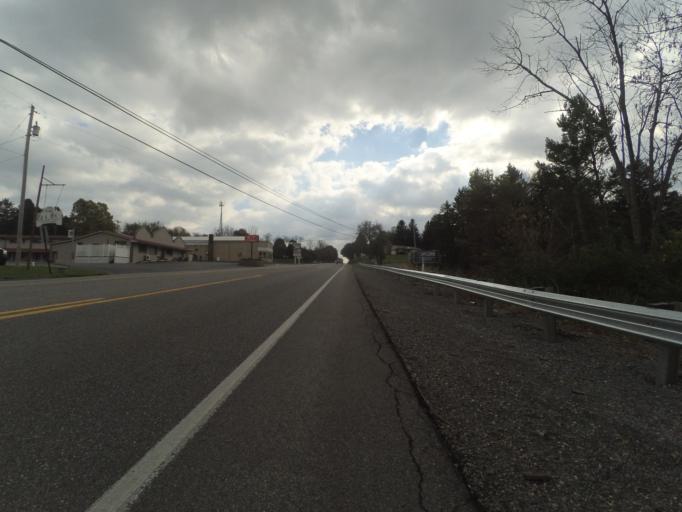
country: US
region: Pennsylvania
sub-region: Centre County
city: Bellefonte
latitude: 40.8941
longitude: -77.7861
